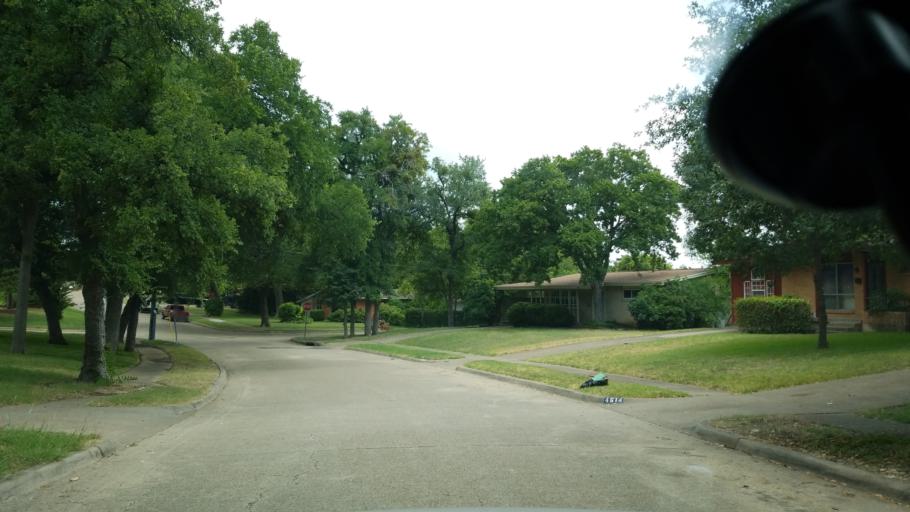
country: US
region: Texas
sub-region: Dallas County
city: Cockrell Hill
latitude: 32.6879
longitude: -96.8545
